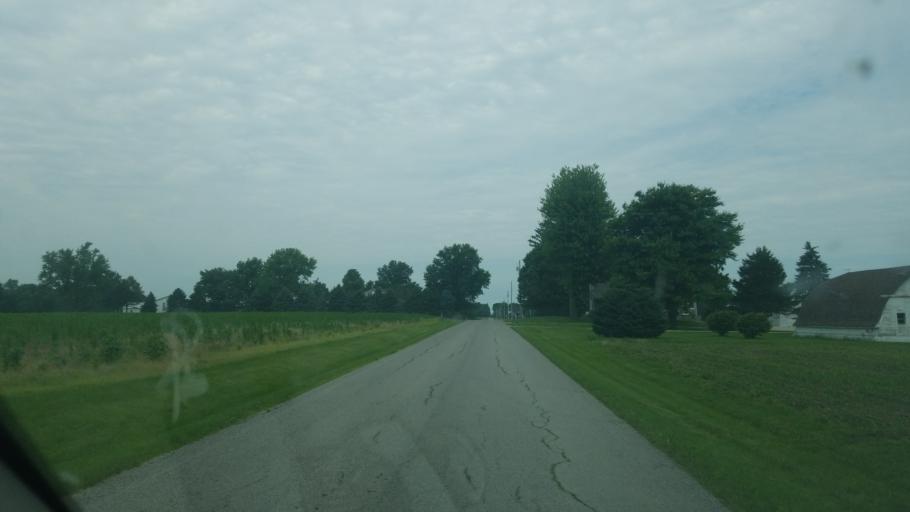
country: US
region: Ohio
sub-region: Seneca County
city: Fostoria
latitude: 41.0502
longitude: -83.4428
